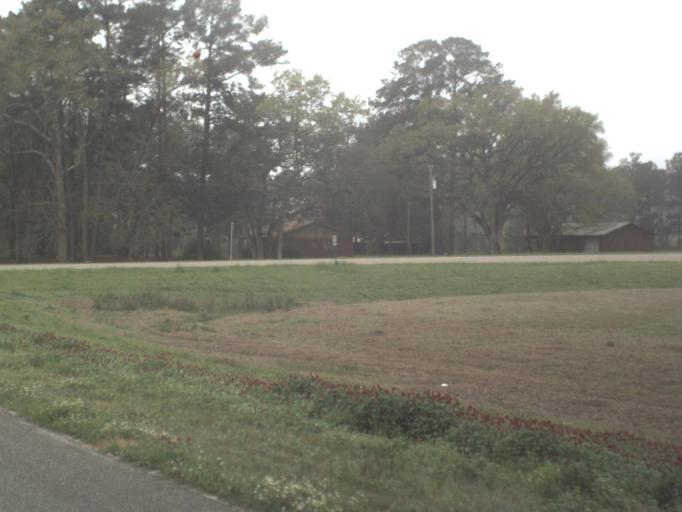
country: US
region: Florida
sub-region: Gadsden County
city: Gretna
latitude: 30.5695
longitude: -84.6735
